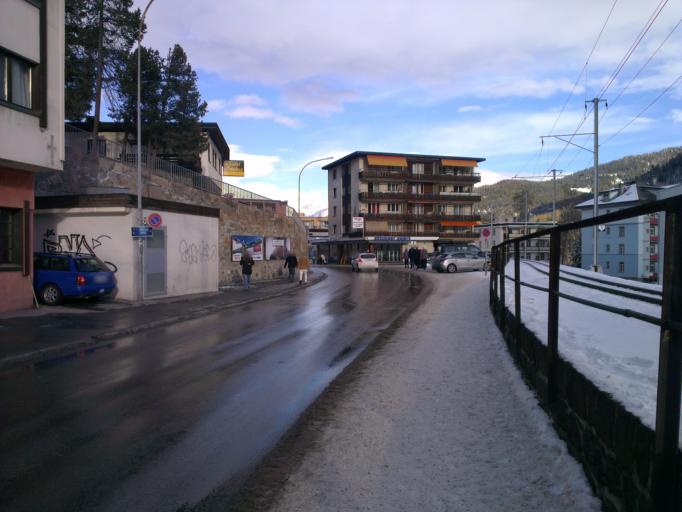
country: CH
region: Grisons
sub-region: Praettigau/Davos District
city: Davos
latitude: 46.7928
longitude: 9.8224
